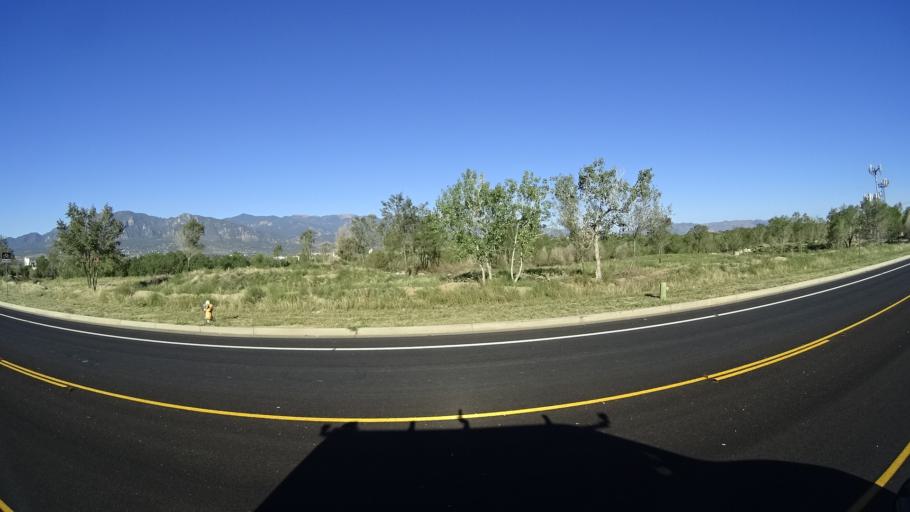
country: US
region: Colorado
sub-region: El Paso County
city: Stratmoor
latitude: 38.7927
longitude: -104.7598
